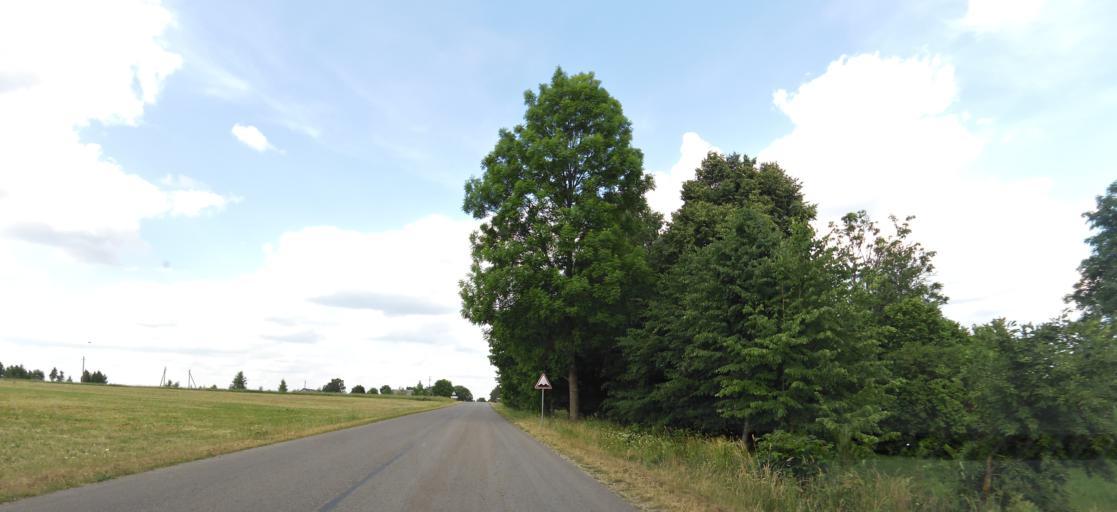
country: LT
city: Skaidiskes
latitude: 54.5300
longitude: 25.6401
